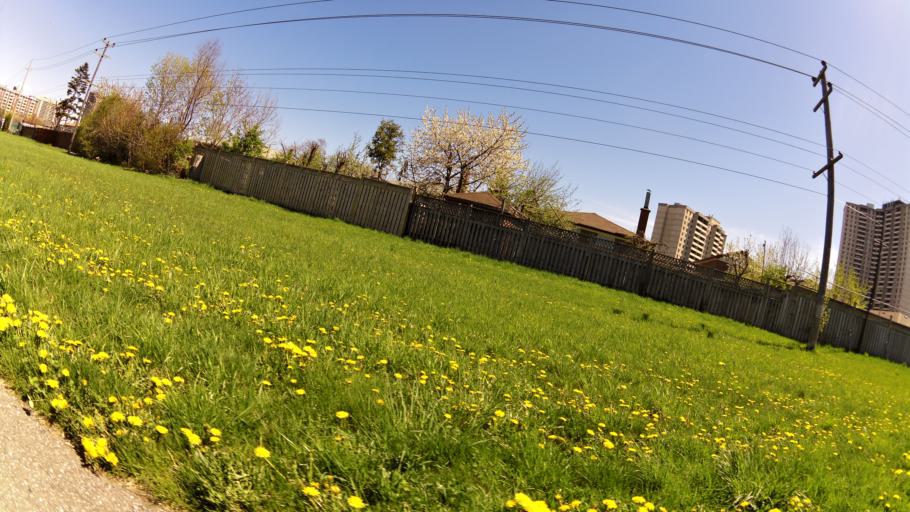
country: CA
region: Ontario
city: Concord
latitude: 43.7608
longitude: -79.5155
